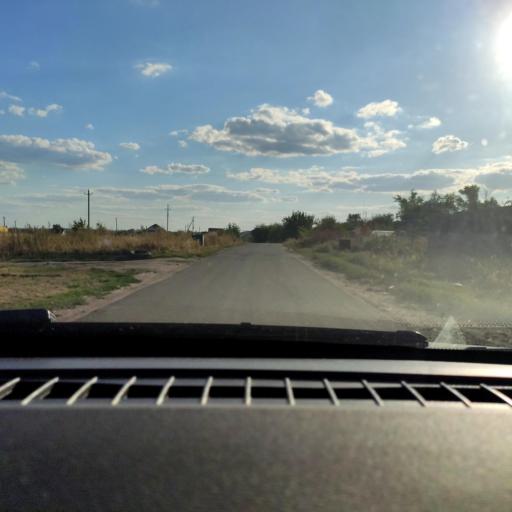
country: RU
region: Voronezj
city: Devitsa
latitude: 51.6457
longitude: 38.9453
